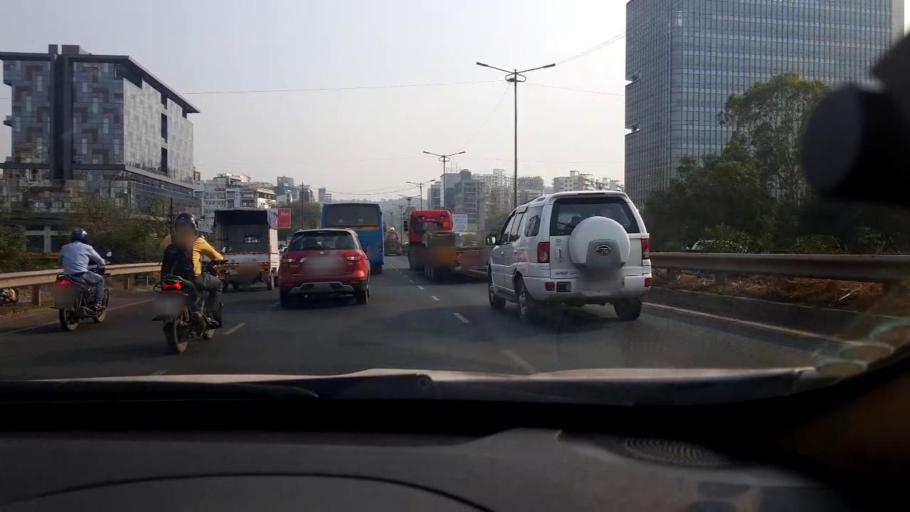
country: IN
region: Maharashtra
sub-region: Pune Division
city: Pimpri
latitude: 18.5584
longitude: 73.7697
